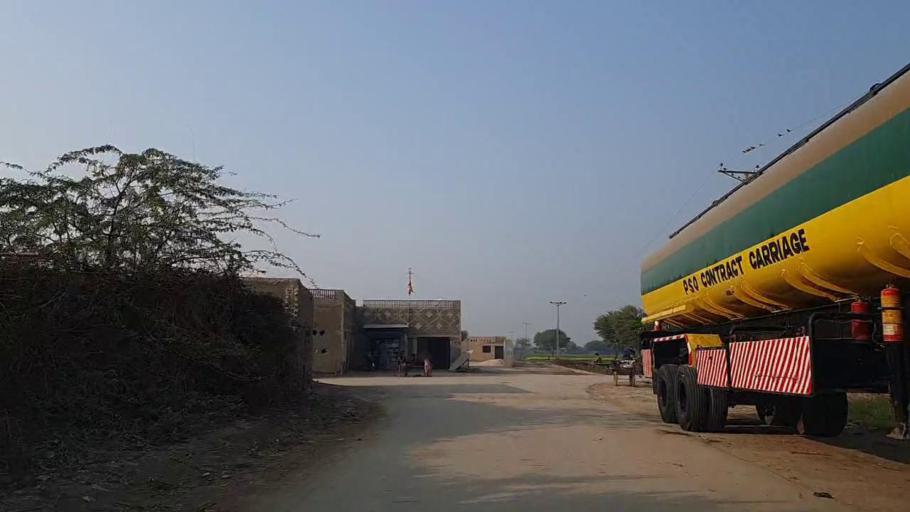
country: PK
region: Sindh
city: Sann
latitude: 26.1259
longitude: 68.1460
